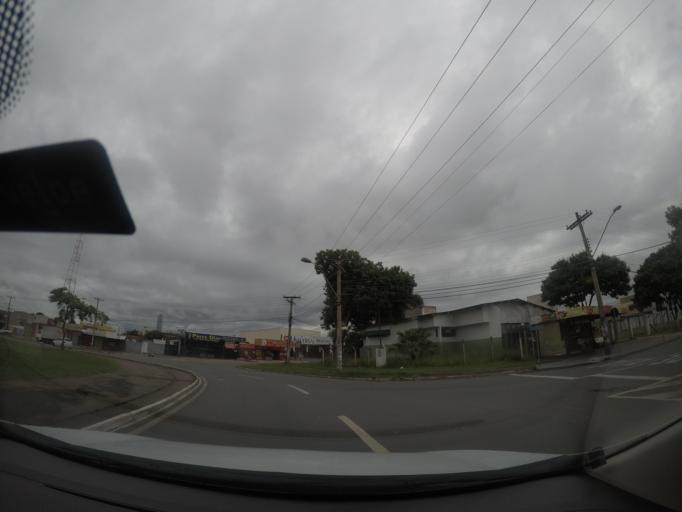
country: BR
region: Goias
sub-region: Goiania
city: Goiania
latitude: -16.7292
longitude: -49.2772
